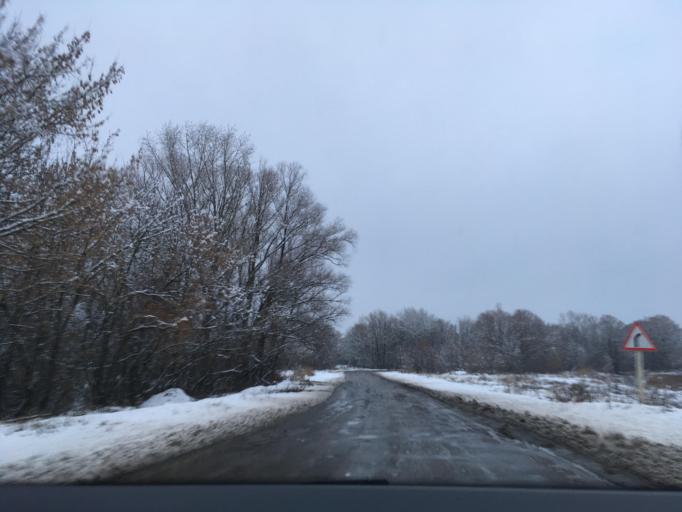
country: RU
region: Voronezj
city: Mitrofanovka
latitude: 50.1343
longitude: 39.9900
